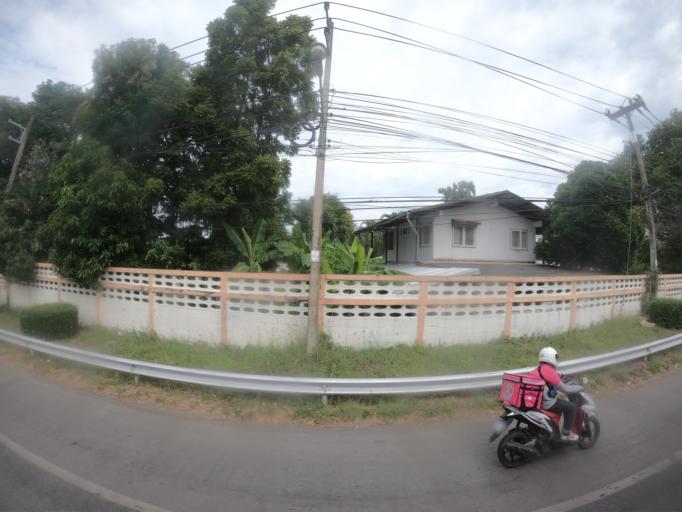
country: TH
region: Maha Sarakham
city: Maha Sarakham
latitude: 16.2033
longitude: 103.2883
